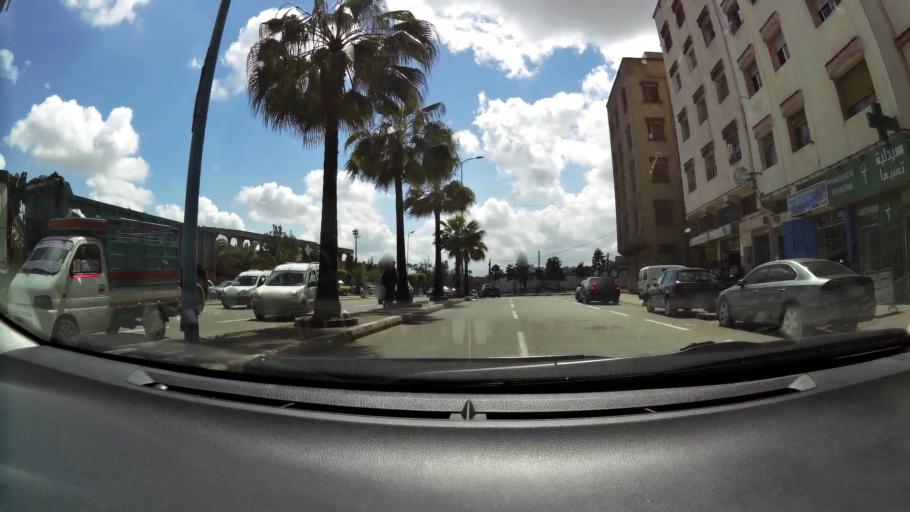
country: MA
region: Grand Casablanca
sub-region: Casablanca
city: Casablanca
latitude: 33.5437
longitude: -7.5614
